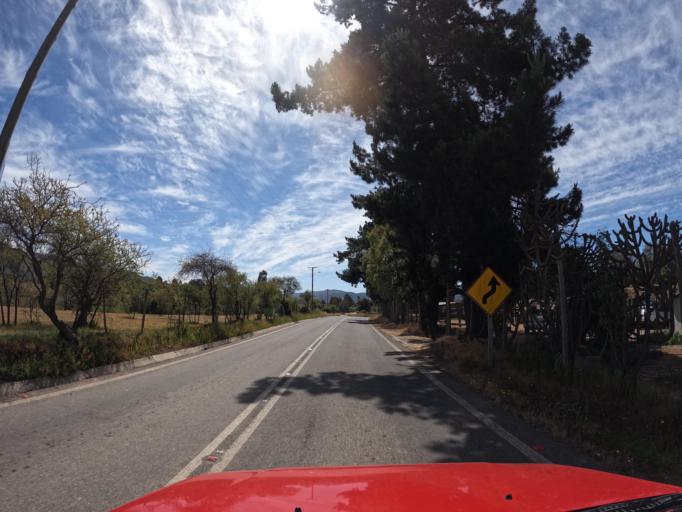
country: CL
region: Maule
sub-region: Provincia de Talca
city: Talca
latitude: -35.0101
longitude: -71.7855
